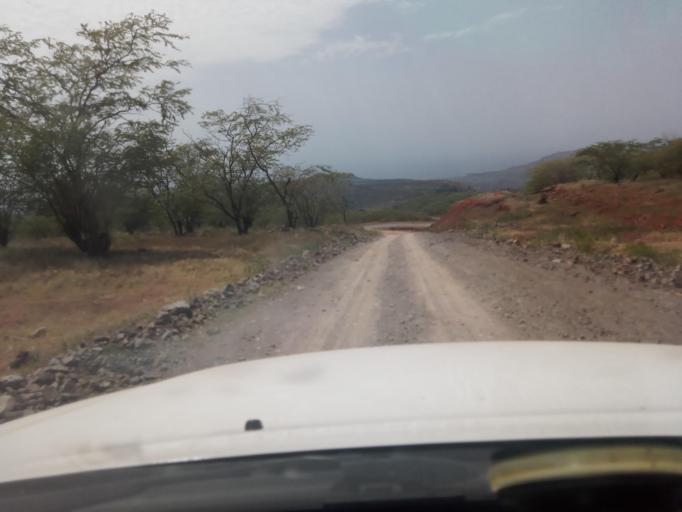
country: CV
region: Sao Domingos
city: Sao Domingos
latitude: 14.9918
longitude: -23.6242
